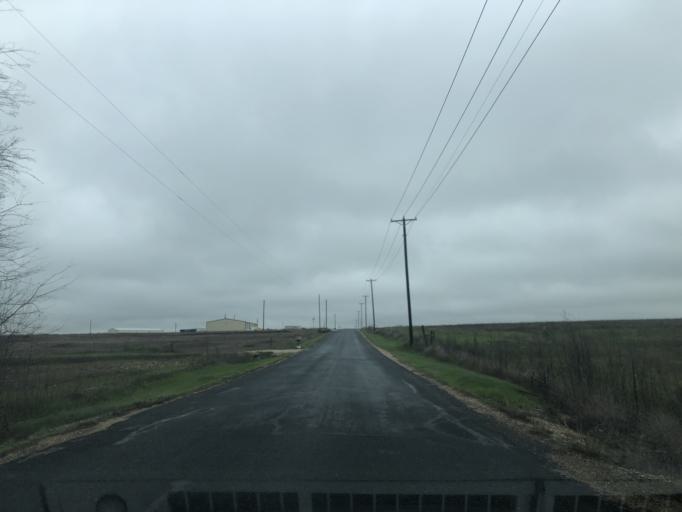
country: US
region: Texas
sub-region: Williamson County
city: Serenada
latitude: 30.7710
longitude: -97.6180
